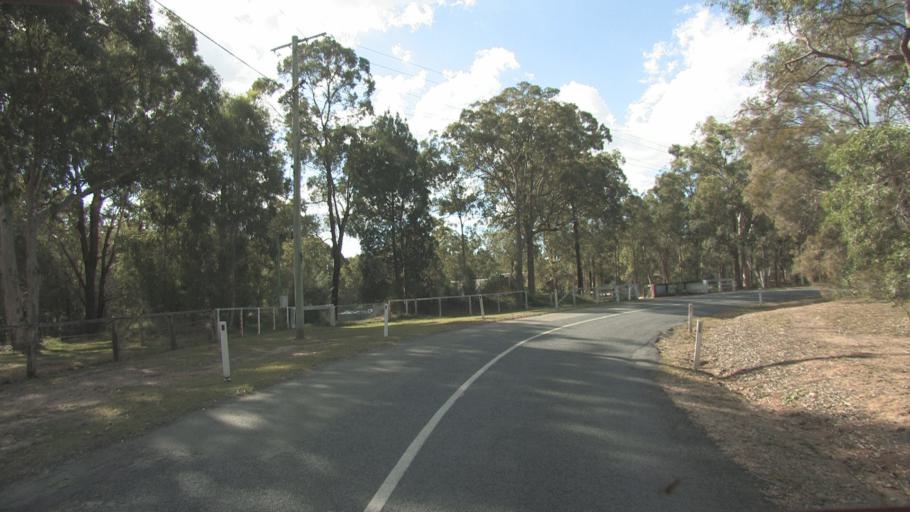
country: AU
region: Queensland
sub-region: Gold Coast
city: Yatala
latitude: -27.6589
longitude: 153.2419
